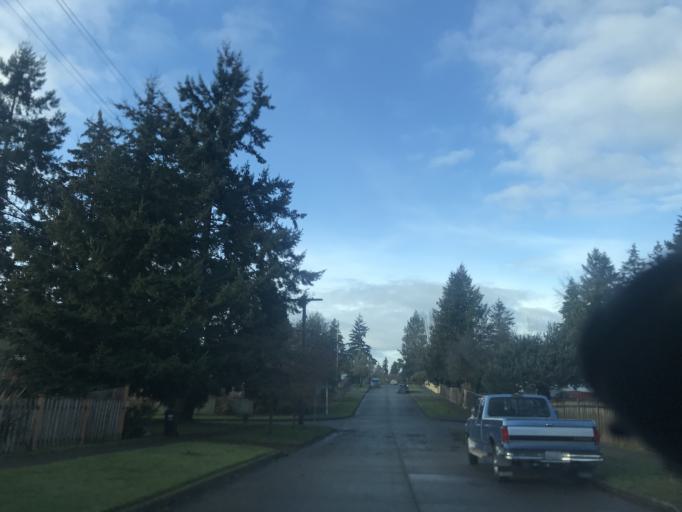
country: US
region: Washington
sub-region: King County
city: White Center
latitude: 47.5265
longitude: -122.3719
